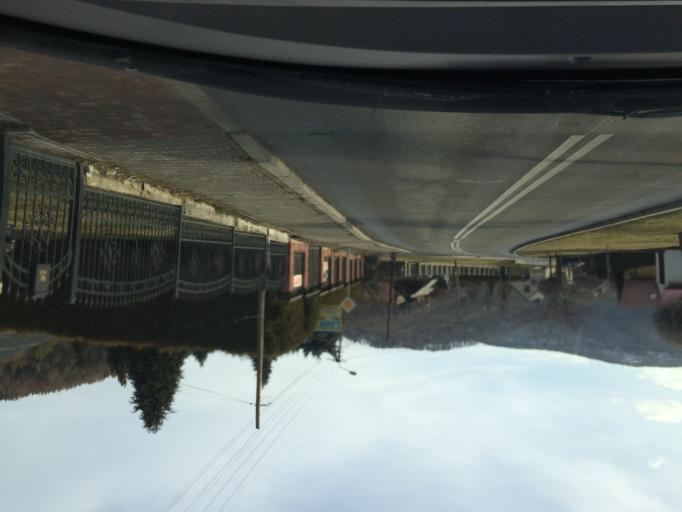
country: PL
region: Silesian Voivodeship
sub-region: Powiat bielski
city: Bystra
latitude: 49.7604
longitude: 19.0477
